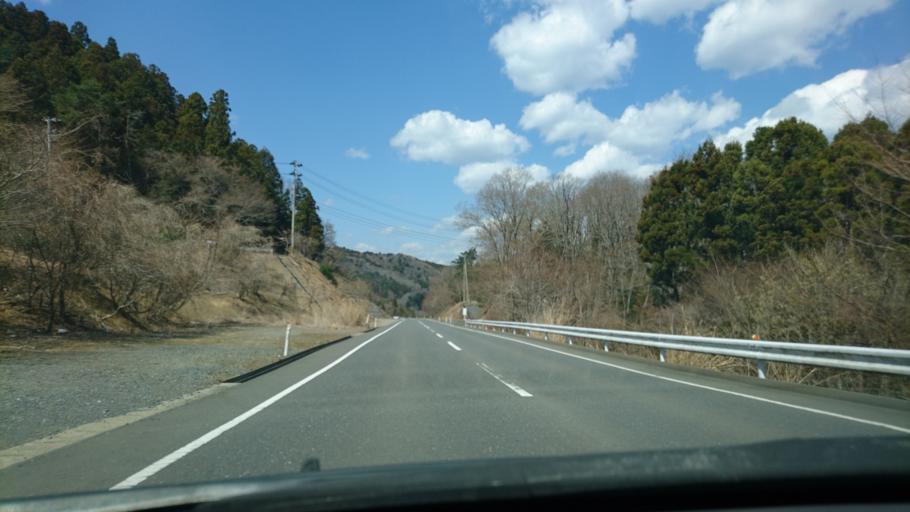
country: JP
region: Miyagi
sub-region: Oshika Gun
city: Onagawa Cho
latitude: 38.4810
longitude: 141.4933
